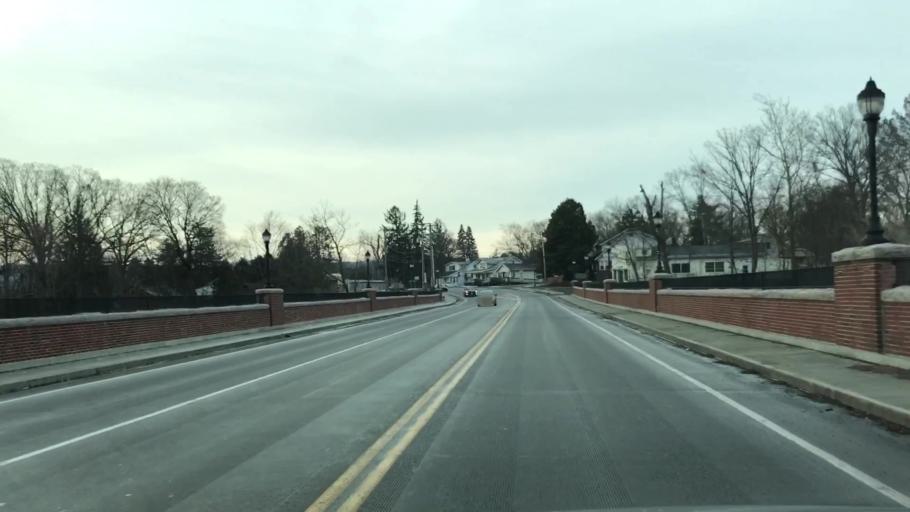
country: US
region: New York
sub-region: Rockland County
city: Stony Point
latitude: 41.2288
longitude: -73.9872
